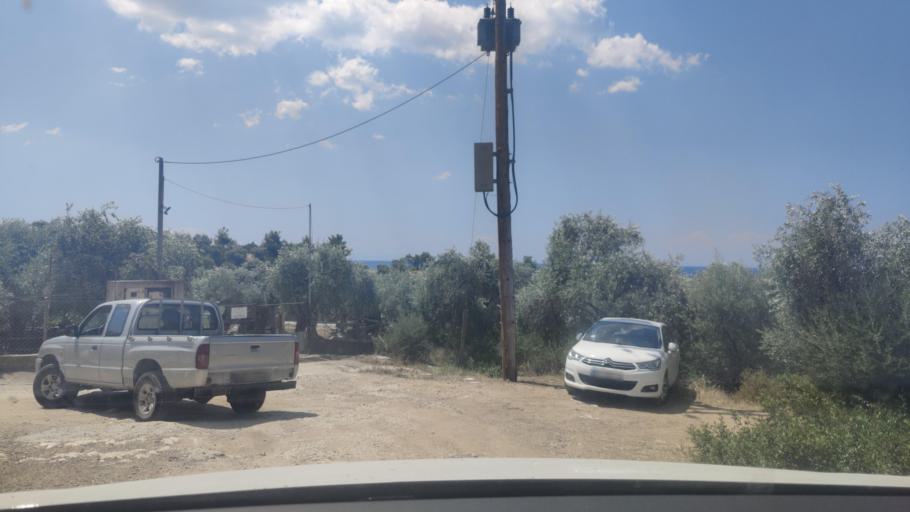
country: GR
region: East Macedonia and Thrace
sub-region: Nomos Kavalas
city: Limenaria
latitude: 40.6384
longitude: 24.5242
